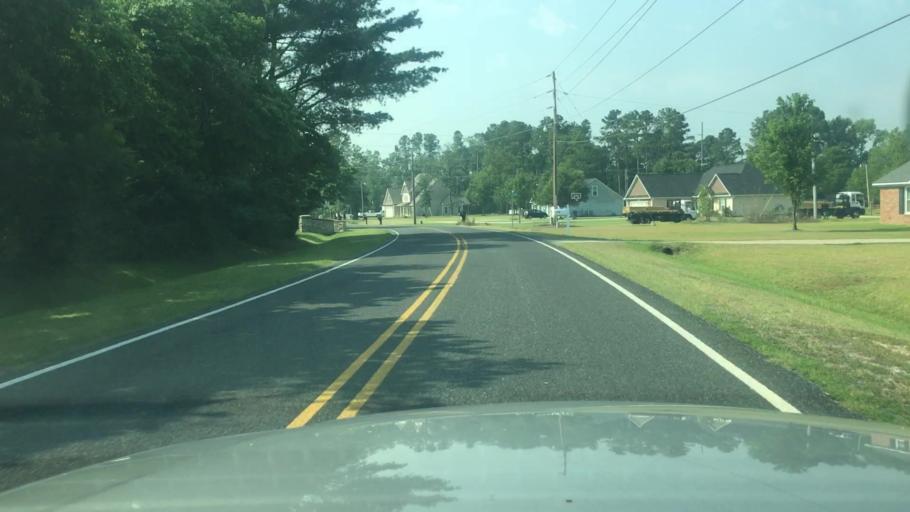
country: US
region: North Carolina
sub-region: Cumberland County
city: Hope Mills
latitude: 34.9048
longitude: -78.8720
